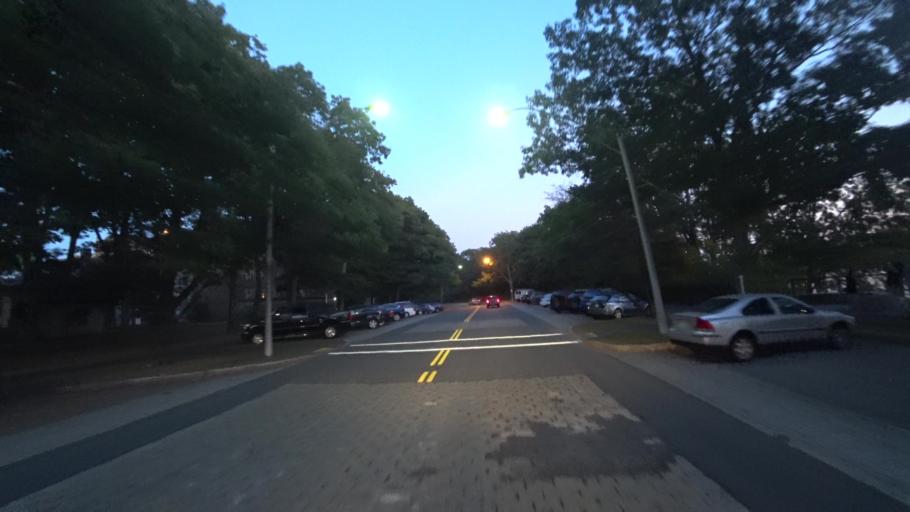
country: US
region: Massachusetts
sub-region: Norfolk County
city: Brookline
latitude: 42.3384
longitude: -71.1568
